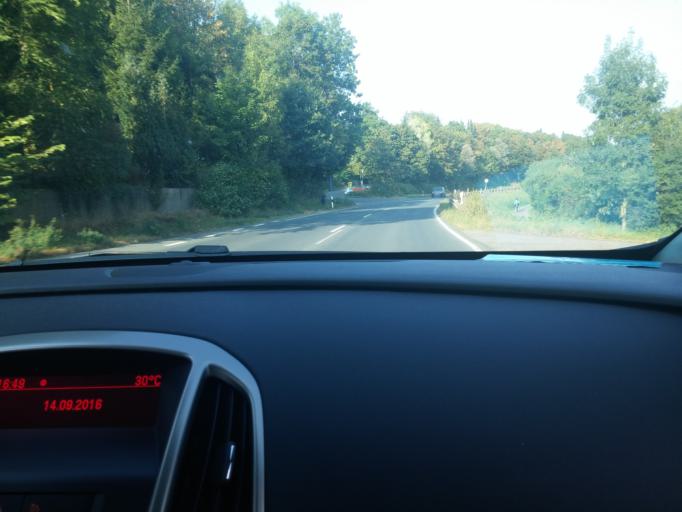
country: DE
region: Bavaria
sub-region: Upper Franconia
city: Coburg
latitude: 50.2628
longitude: 10.9361
